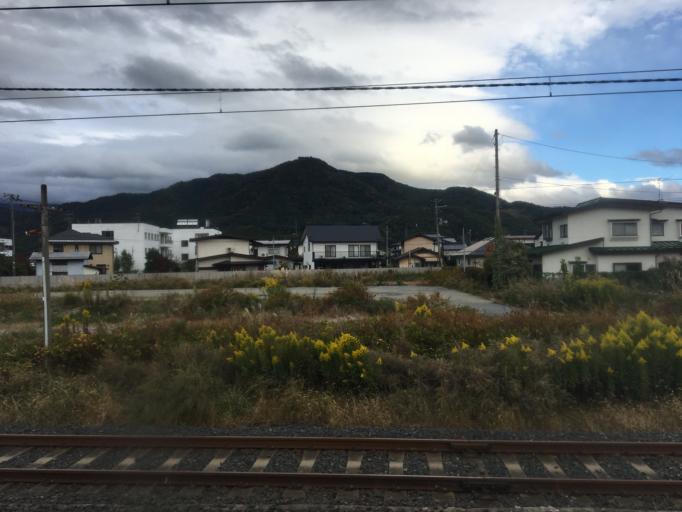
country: JP
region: Yamagata
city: Kaminoyama
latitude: 38.1508
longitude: 140.2777
